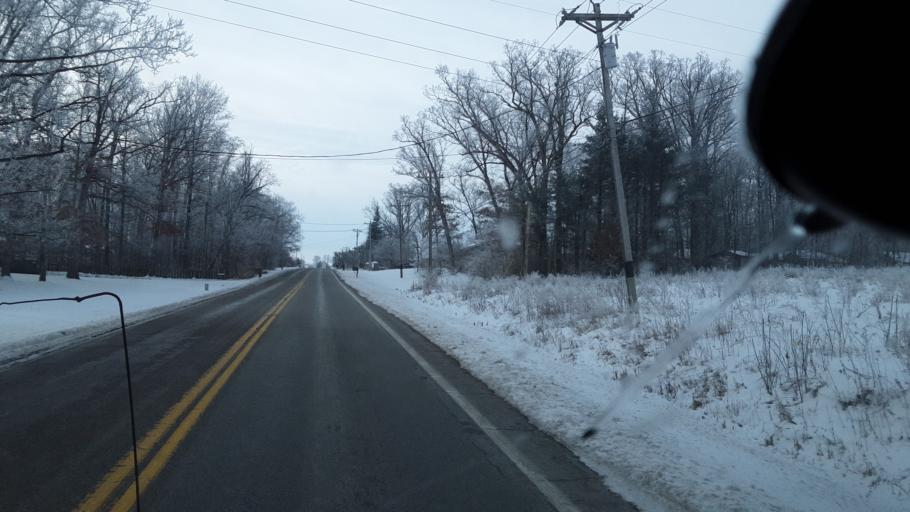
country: US
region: Ohio
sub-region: Union County
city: Marysville
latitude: 40.2047
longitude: -83.3769
